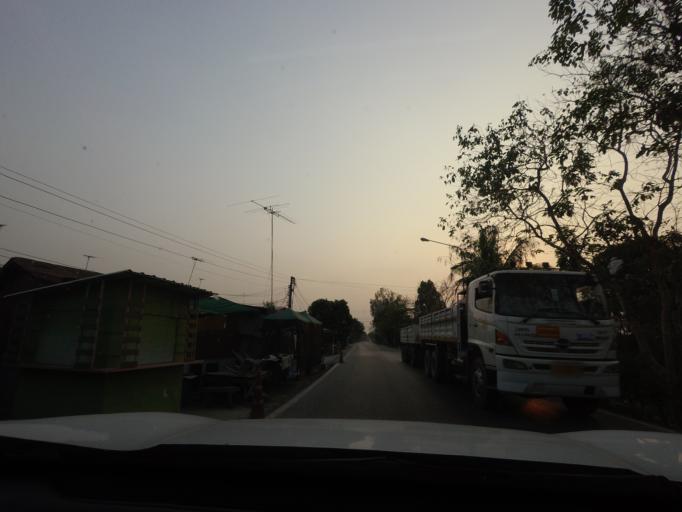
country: TH
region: Nakhon Nayok
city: Ongkharak
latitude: 14.1790
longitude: 101.0626
